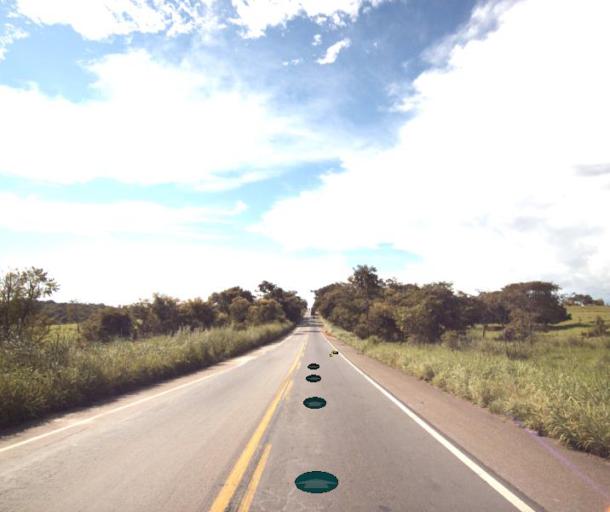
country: BR
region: Goias
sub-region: Jaragua
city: Jaragua
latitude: -15.5716
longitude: -49.4195
